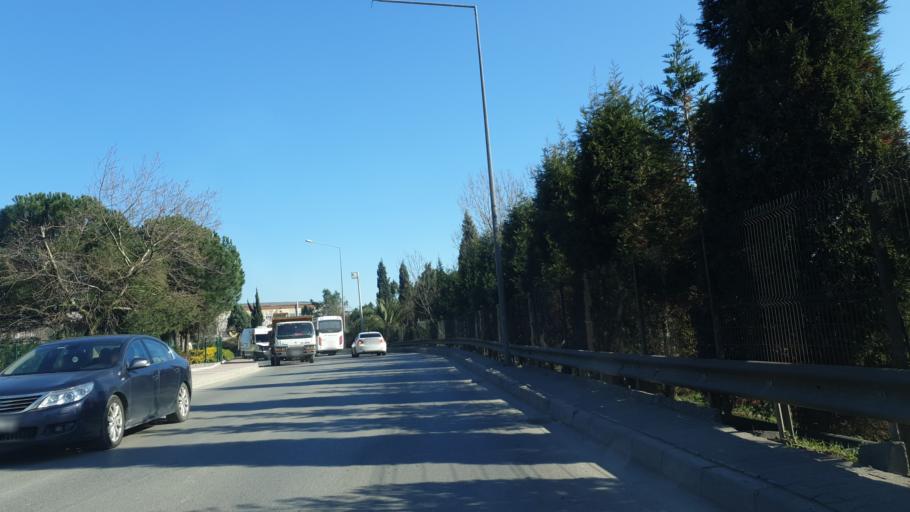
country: TR
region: Istanbul
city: Icmeler
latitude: 40.8792
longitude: 29.3586
